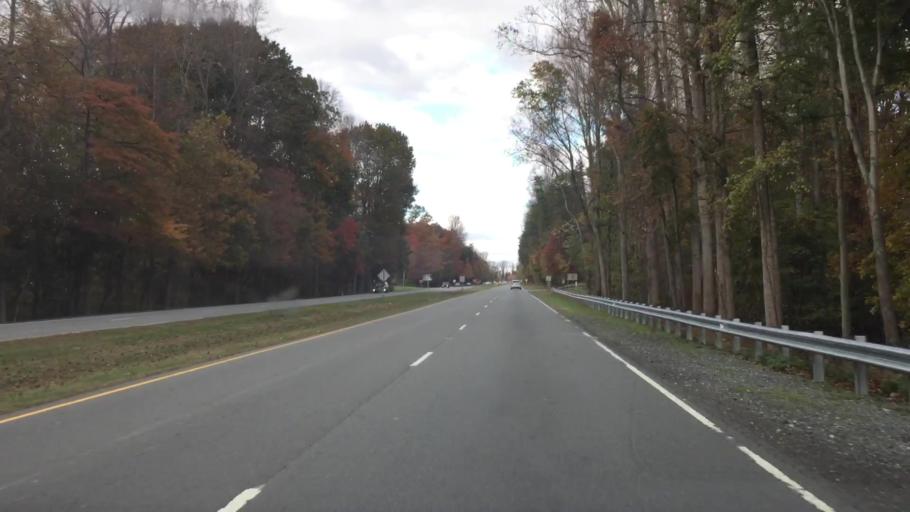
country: US
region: North Carolina
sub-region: Forsyth County
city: Winston-Salem
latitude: 36.1061
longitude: -80.1915
